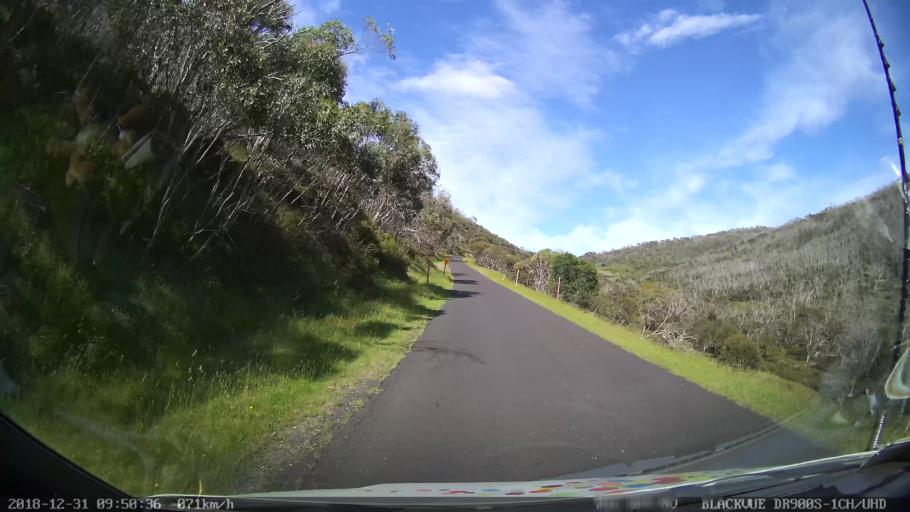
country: AU
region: New South Wales
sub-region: Snowy River
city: Jindabyne
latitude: -36.5210
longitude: 148.2711
